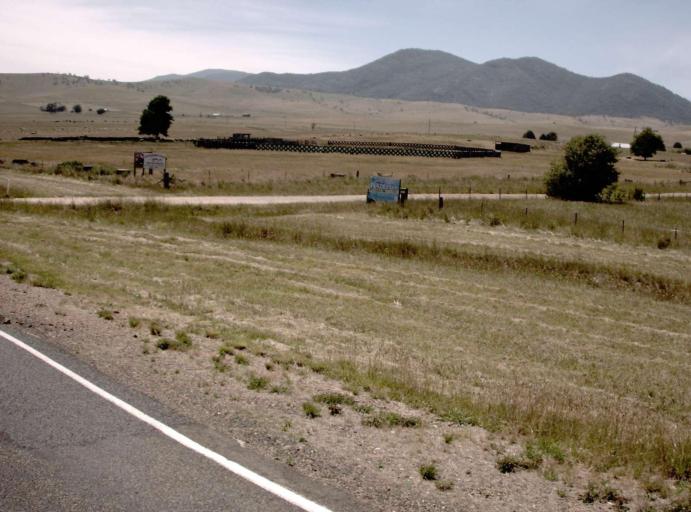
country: AU
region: Victoria
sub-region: Alpine
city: Mount Beauty
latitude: -37.0033
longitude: 147.6668
